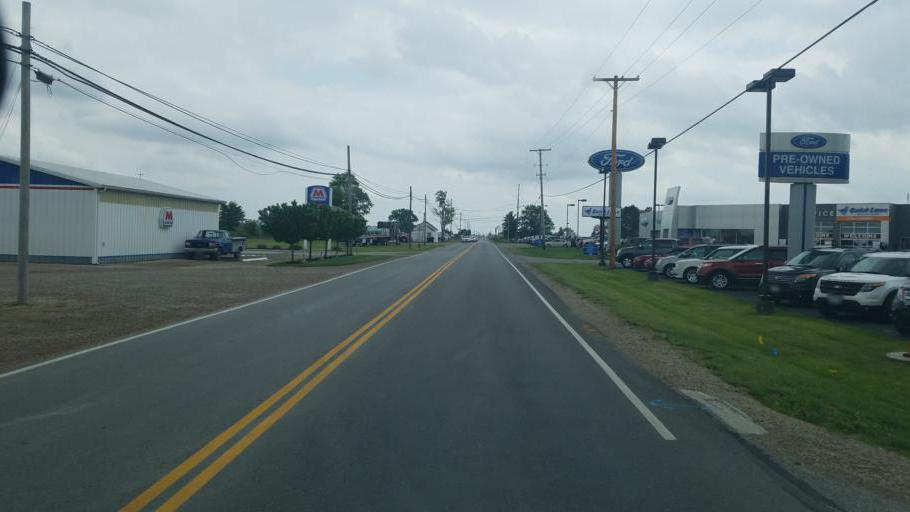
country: US
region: Ohio
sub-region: Union County
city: Marysville
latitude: 40.2295
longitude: -83.3475
